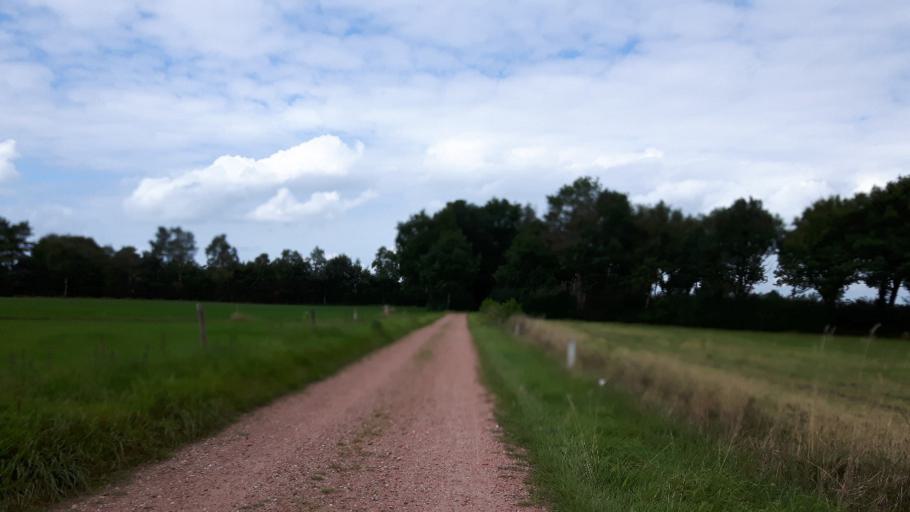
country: NL
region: Groningen
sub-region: Gemeente Leek
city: Leek
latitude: 53.0836
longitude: 6.3223
